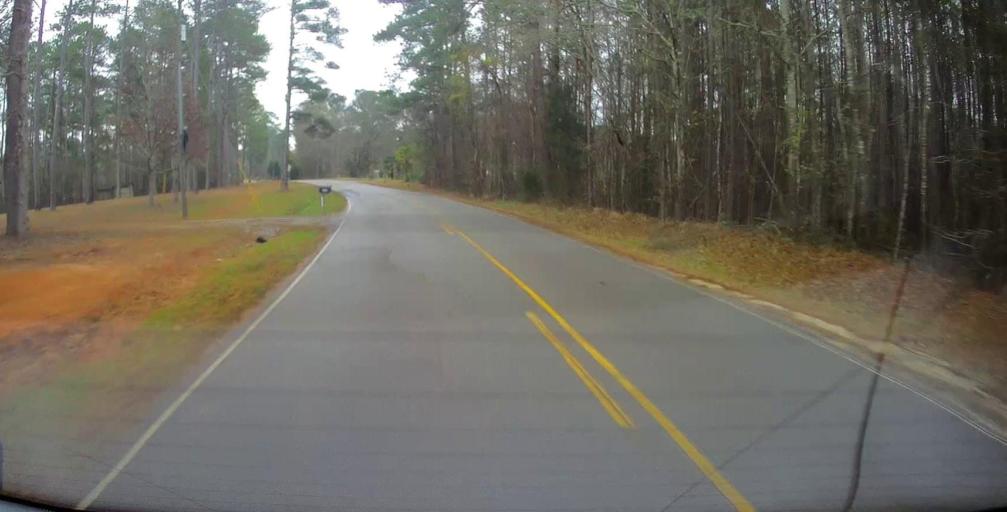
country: US
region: Georgia
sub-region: Monroe County
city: Forsyth
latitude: 33.0188
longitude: -83.8536
